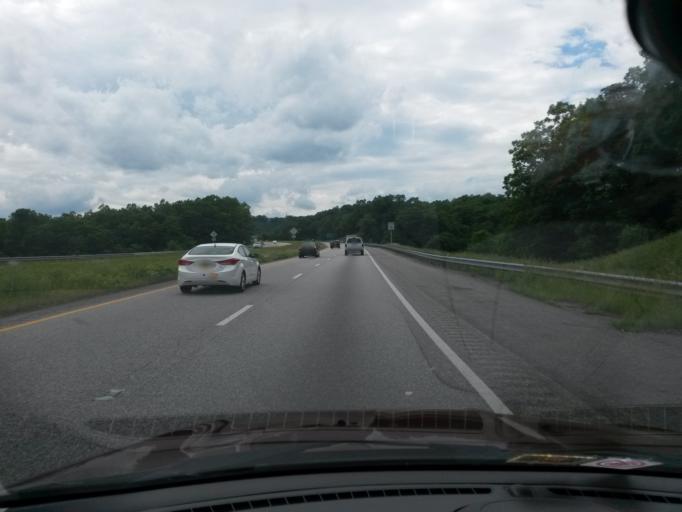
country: US
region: Virginia
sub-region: Alleghany County
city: Clifton Forge
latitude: 37.8287
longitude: -79.8051
